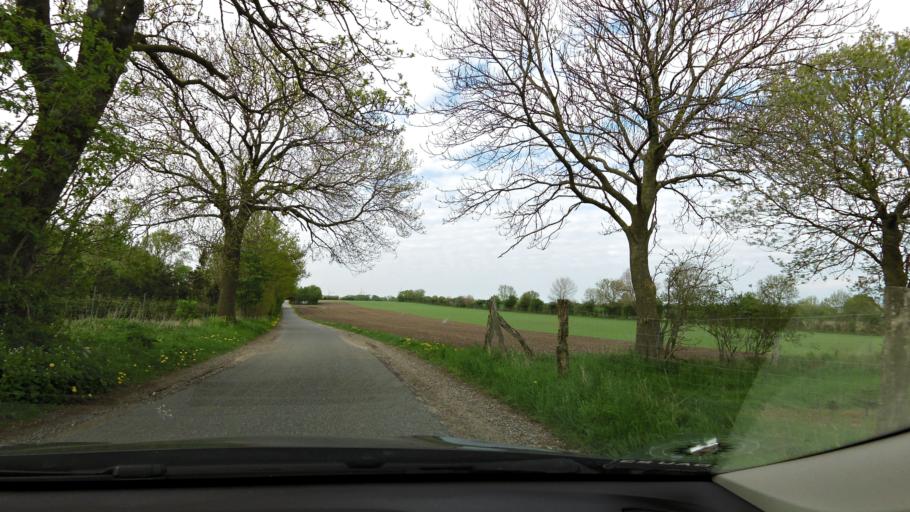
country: DK
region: South Denmark
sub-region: Nyborg Kommune
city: Nyborg
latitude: 55.2494
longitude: 10.7093
